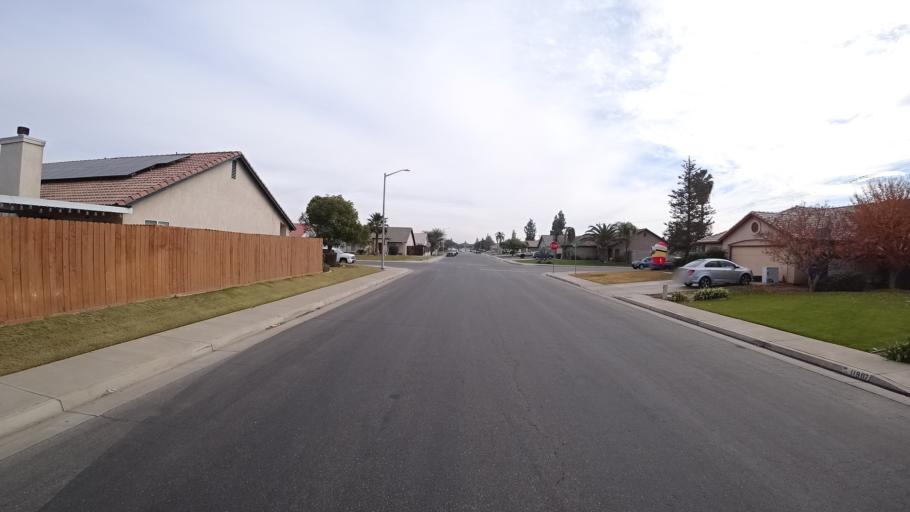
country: US
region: California
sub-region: Kern County
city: Rosedale
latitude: 35.3986
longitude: -119.1346
